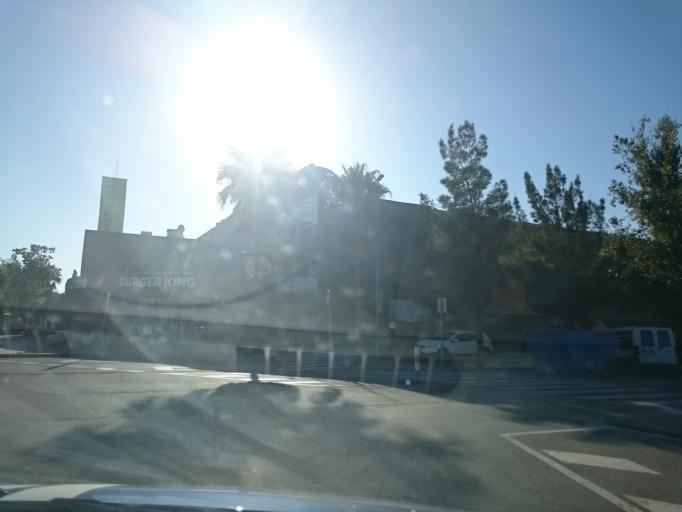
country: ES
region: Catalonia
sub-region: Provincia de Barcelona
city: Gava
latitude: 41.2955
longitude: 2.0092
